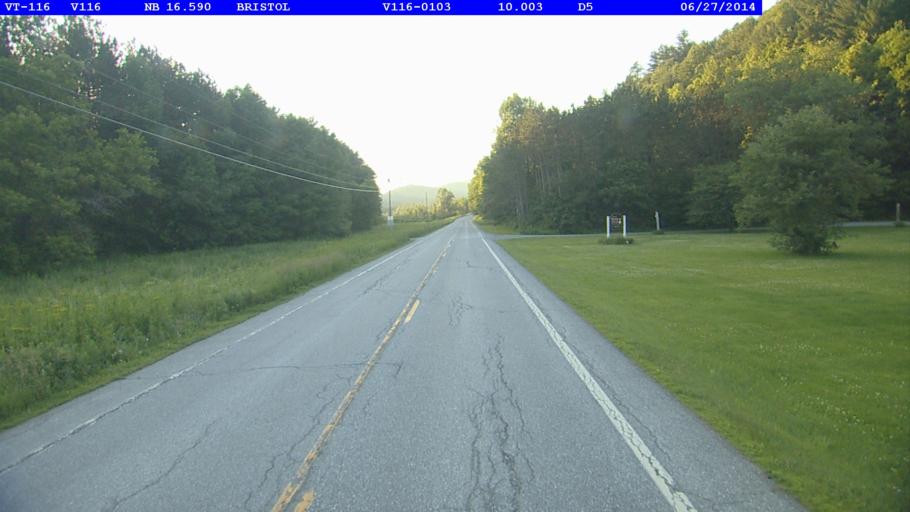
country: US
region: Vermont
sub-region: Addison County
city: Bristol
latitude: 44.1547
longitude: -73.0465
